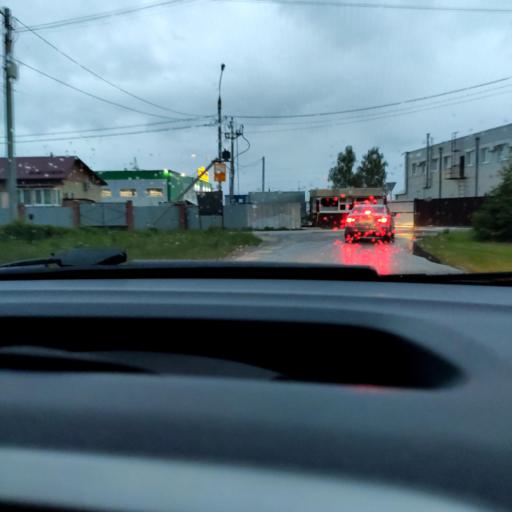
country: RU
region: Samara
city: Tol'yatti
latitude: 53.5436
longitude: 49.3799
